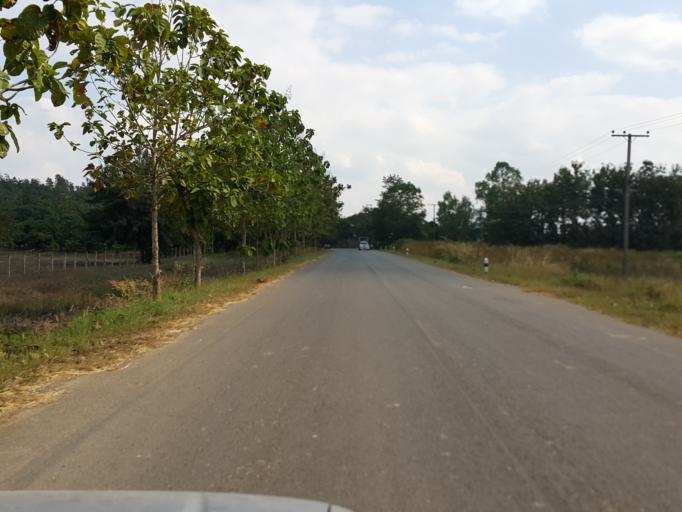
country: TH
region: Sukhothai
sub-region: Amphoe Si Satchanalai
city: Si Satchanalai
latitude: 17.4604
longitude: 99.6650
